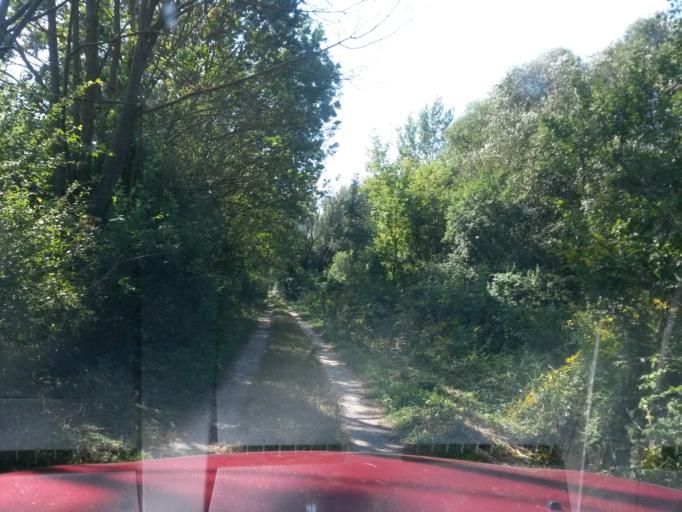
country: HU
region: Borsod-Abauj-Zemplen
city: Gonc
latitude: 48.5404
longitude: 21.1557
